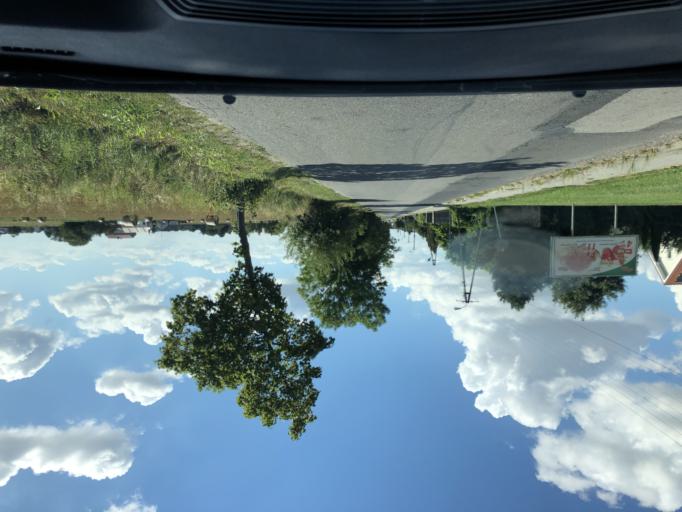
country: PL
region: Lodz Voivodeship
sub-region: Powiat wieruszowski
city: Czastary
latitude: 51.2587
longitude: 18.3243
